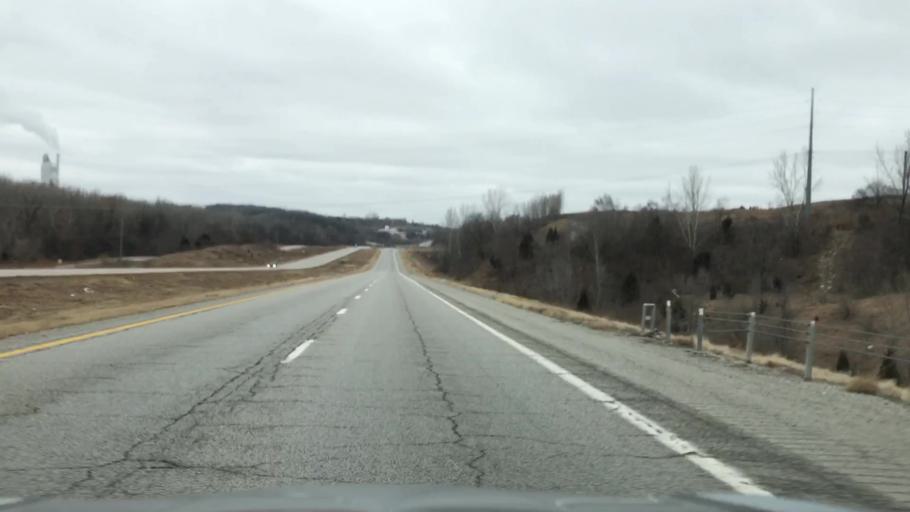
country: US
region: Missouri
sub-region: Jackson County
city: East Independence
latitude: 39.1346
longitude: -94.3845
